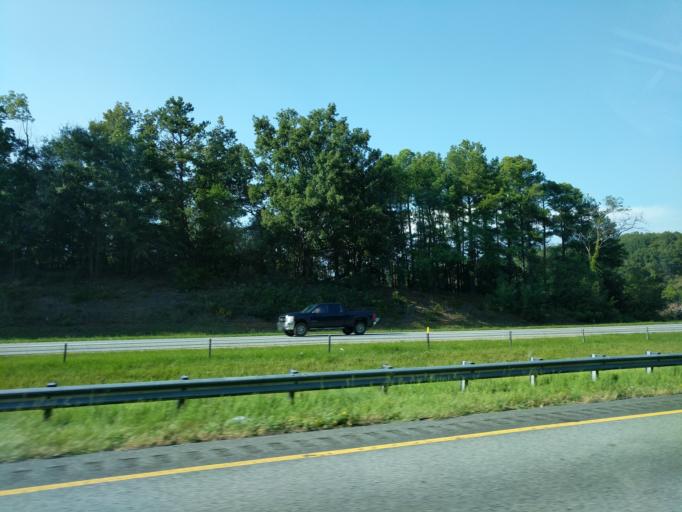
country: US
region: South Carolina
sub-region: Anderson County
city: Centerville
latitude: 34.5365
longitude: -82.8246
